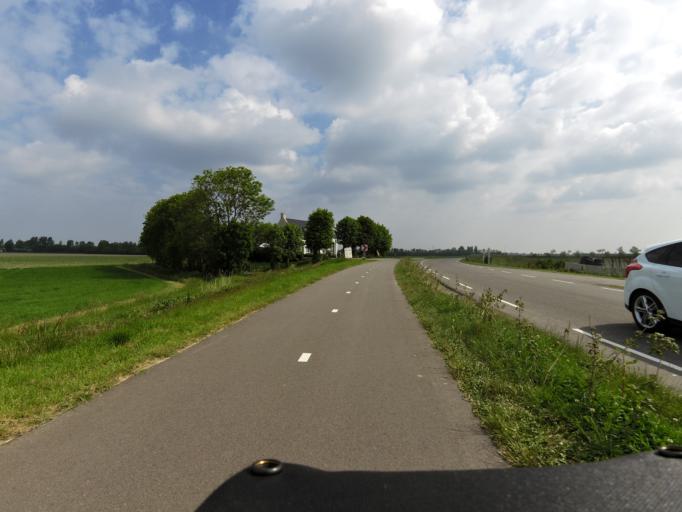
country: NL
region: Zeeland
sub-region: Gemeente Noord-Beveland
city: Kamperland
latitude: 51.5829
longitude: 3.7207
